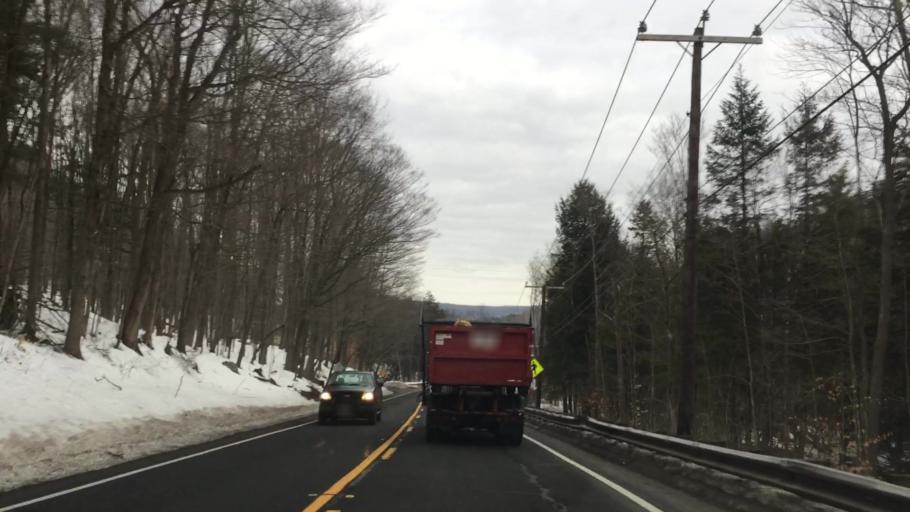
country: US
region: Massachusetts
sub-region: Berkshire County
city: Hinsdale
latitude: 42.4558
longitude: -73.1292
